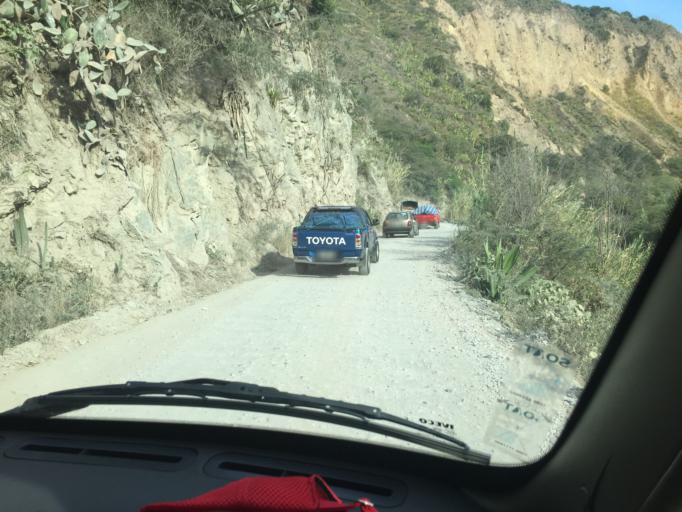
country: EC
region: Carchi
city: El Angel
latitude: 0.5979
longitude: -78.1373
